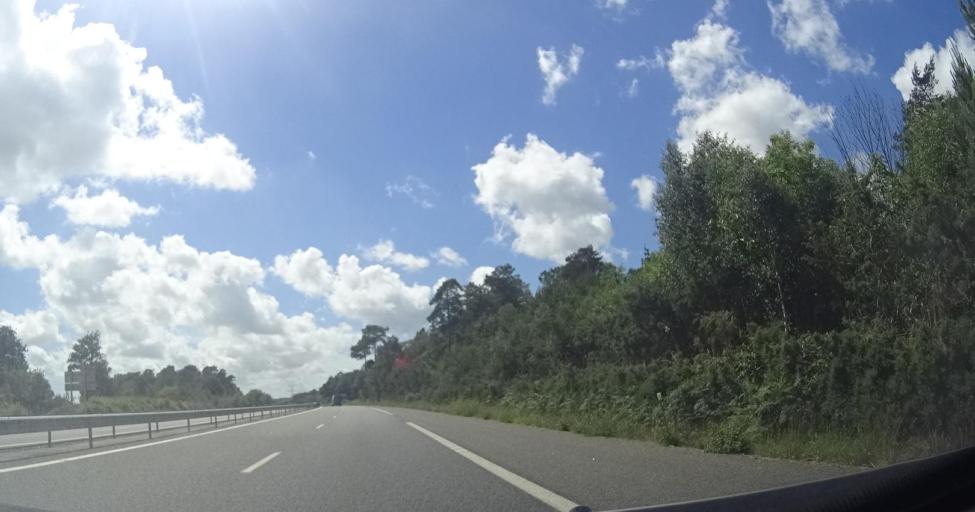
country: FR
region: Brittany
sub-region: Departement du Morbihan
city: Pluherlin
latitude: 47.6700
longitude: -2.3402
